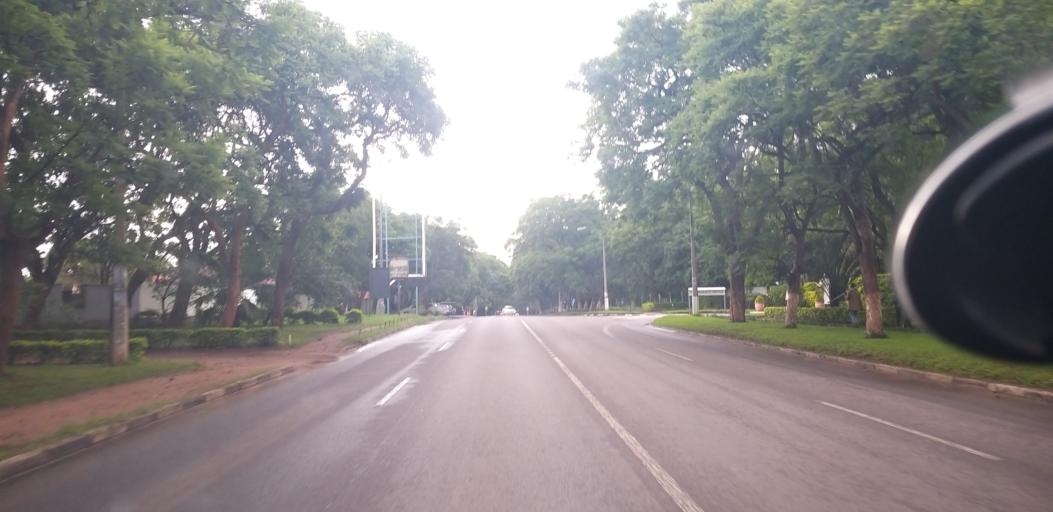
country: ZM
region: Lusaka
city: Lusaka
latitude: -15.4165
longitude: 28.3017
